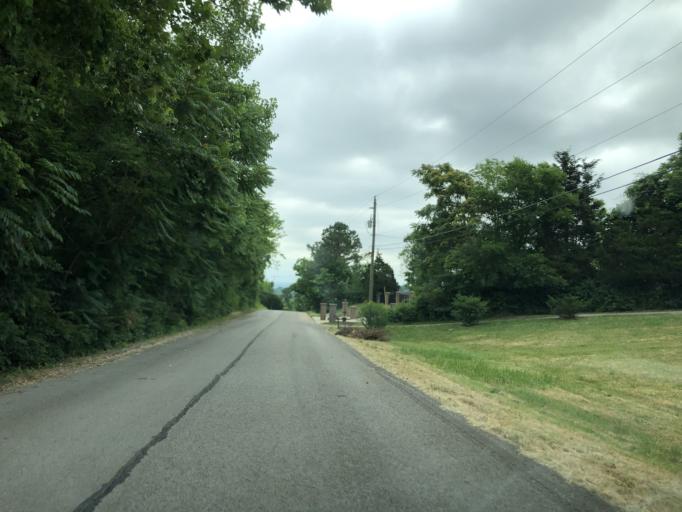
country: US
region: Tennessee
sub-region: Davidson County
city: Goodlettsville
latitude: 36.2901
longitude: -86.7533
